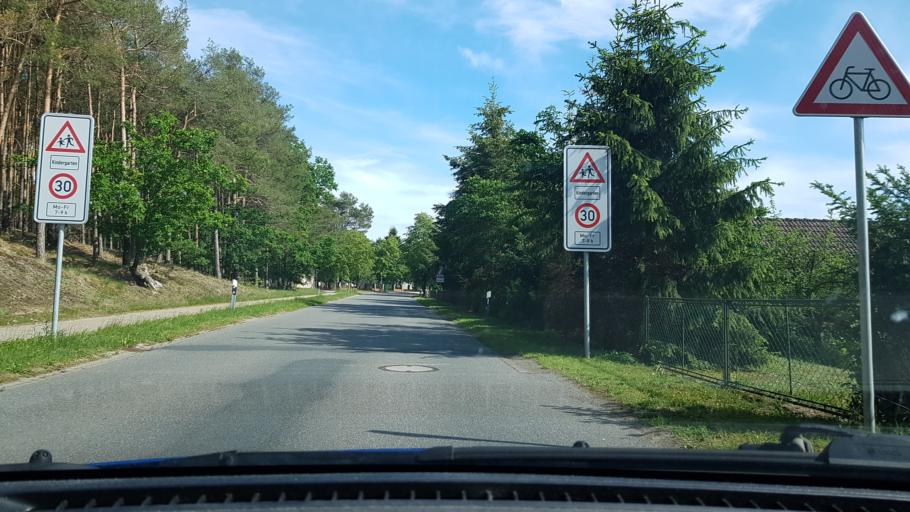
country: DE
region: Lower Saxony
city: Neu Darchau
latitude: 53.2914
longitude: 10.9289
